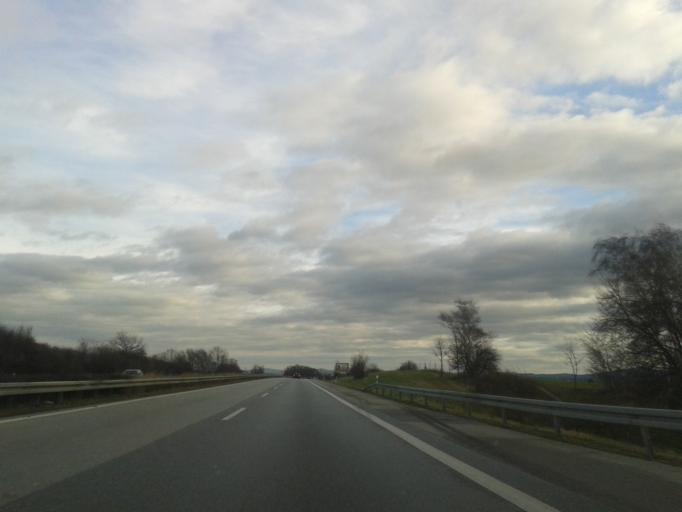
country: DE
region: Saxony
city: Bautzen
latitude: 51.1882
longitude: 14.3784
